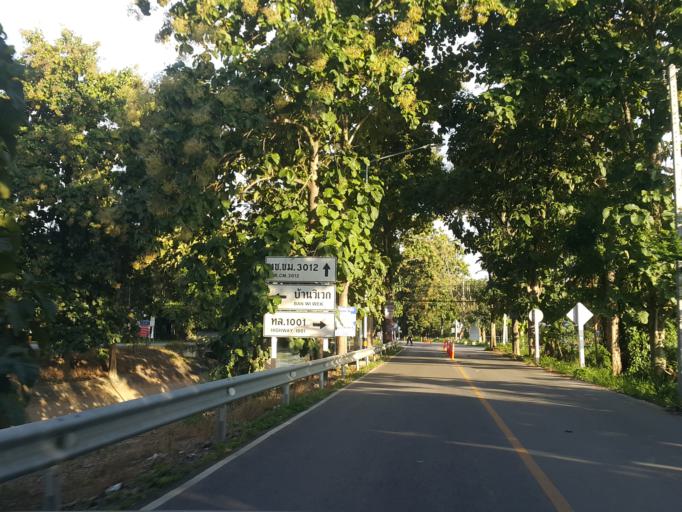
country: TH
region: Chiang Mai
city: San Sai
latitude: 18.9046
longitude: 99.0152
